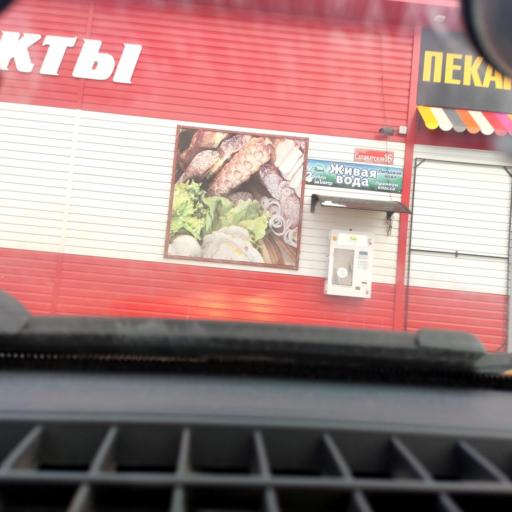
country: RU
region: Bashkortostan
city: Iglino
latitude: 54.8239
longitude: 56.4396
